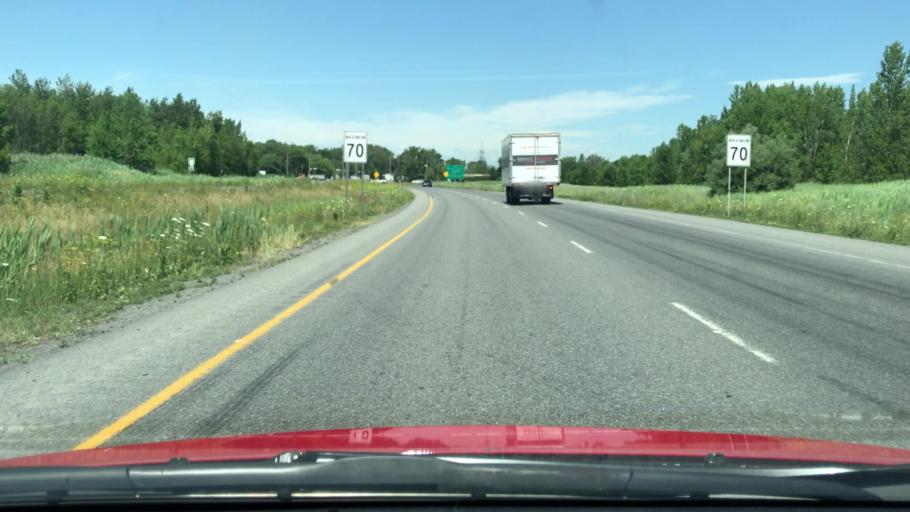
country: CA
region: Quebec
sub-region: Monteregie
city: Saint-Constant
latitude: 45.3914
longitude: -73.6037
